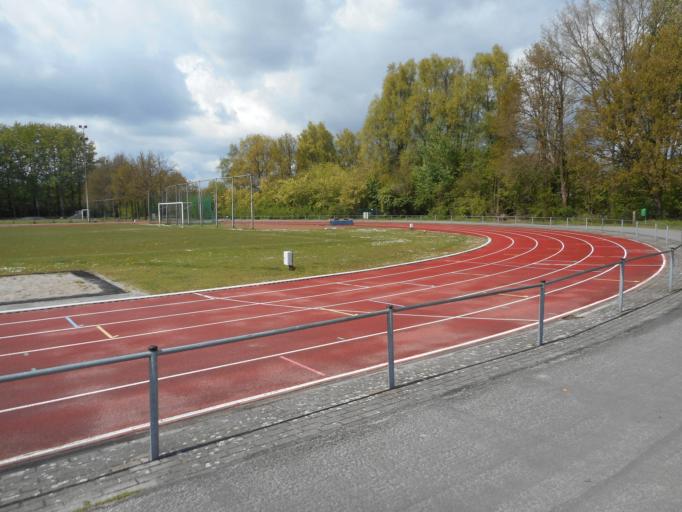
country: BE
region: Flanders
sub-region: Provincie Antwerpen
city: Bornem
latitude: 51.0901
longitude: 4.2461
